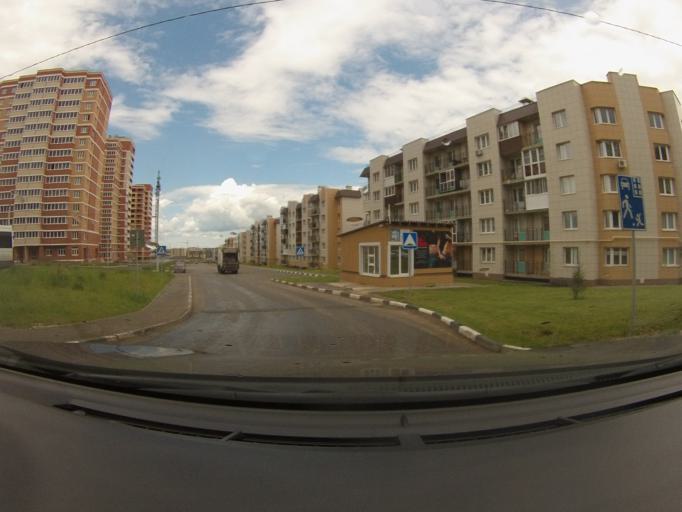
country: RU
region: Tula
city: Tula
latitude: 54.1723
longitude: 37.6542
